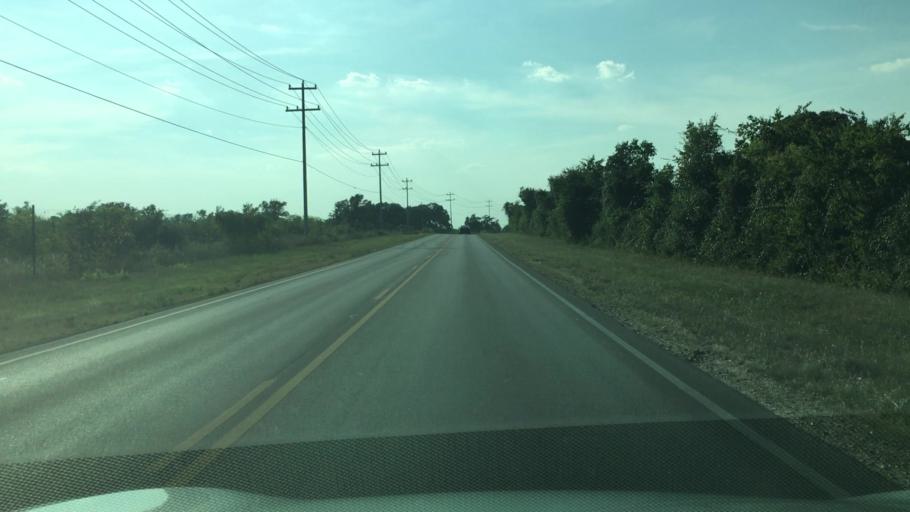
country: US
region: Texas
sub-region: Hays County
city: Buda
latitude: 30.0997
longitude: -97.9353
